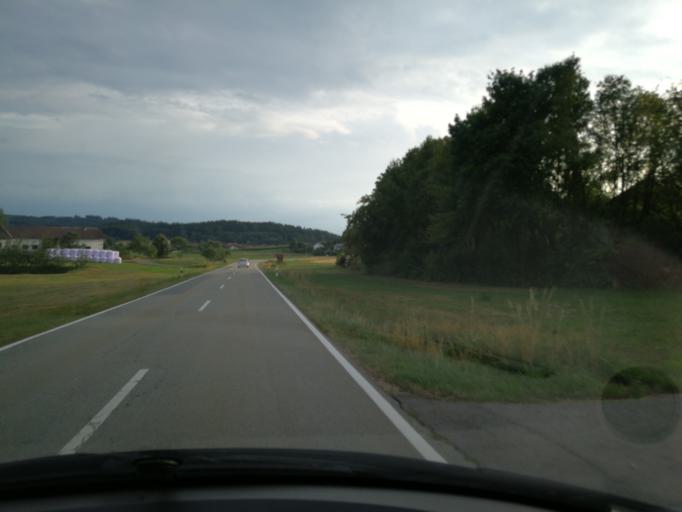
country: DE
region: Bavaria
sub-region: Lower Bavaria
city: Wiesenfelden
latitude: 49.0539
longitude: 12.5735
